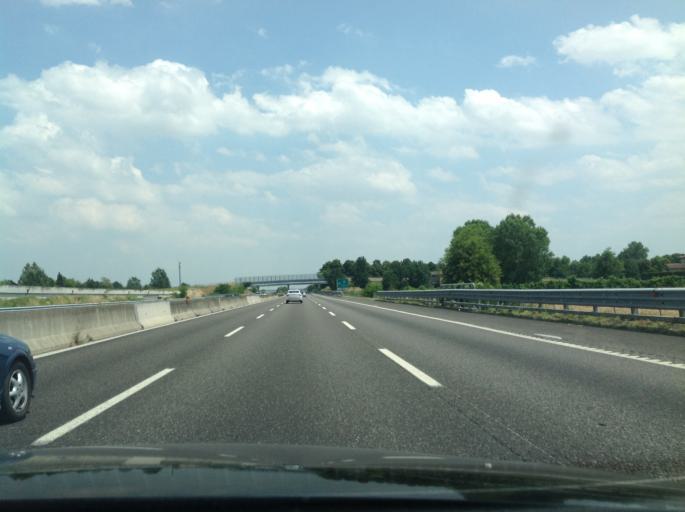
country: IT
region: Emilia-Romagna
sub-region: Provincia di Parma
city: Fontanellato
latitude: 44.8775
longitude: 10.1642
